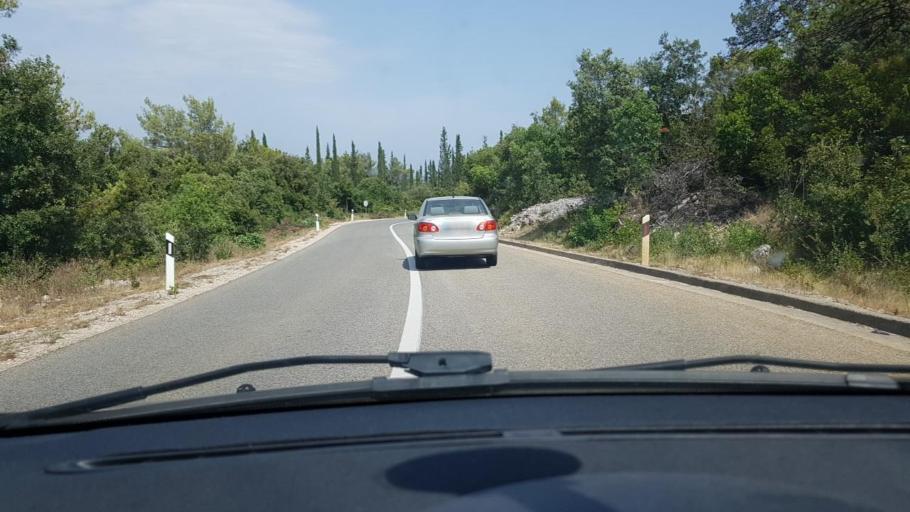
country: HR
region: Dubrovacko-Neretvanska
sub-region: Grad Korcula
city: Zrnovo
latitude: 42.9381
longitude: 17.0922
